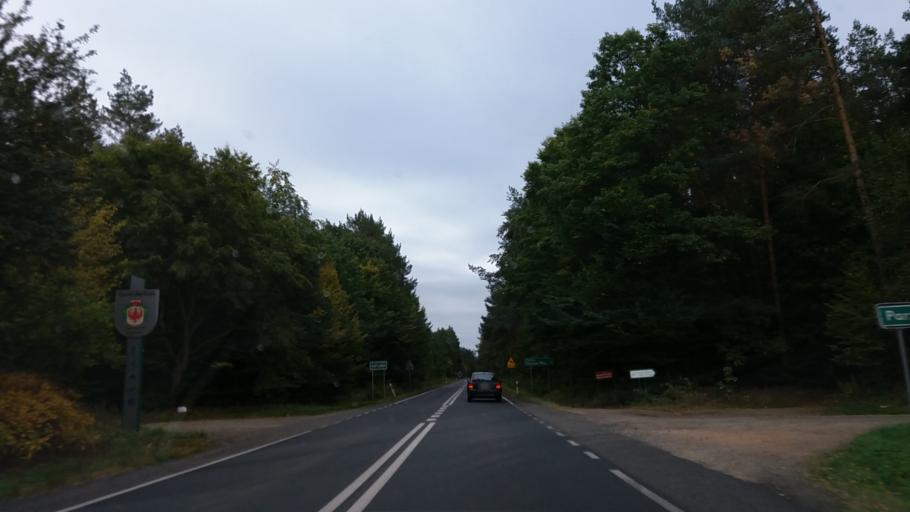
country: PL
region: Lubusz
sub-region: Powiat gorzowski
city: Klodawa
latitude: 52.8781
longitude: 15.1968
